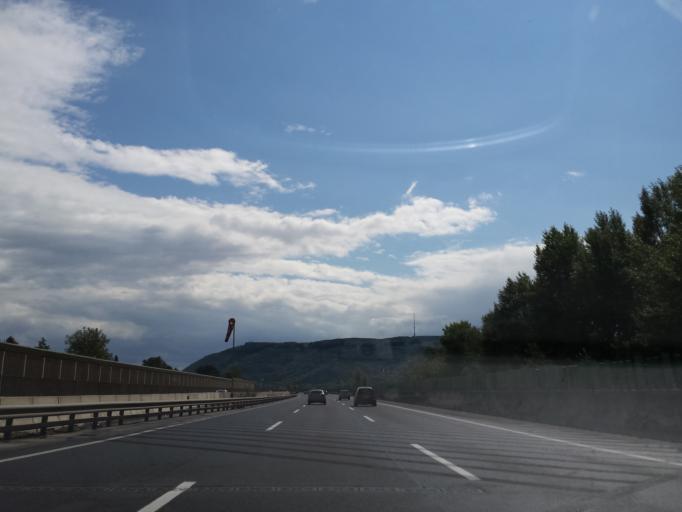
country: AT
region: Lower Austria
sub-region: Politischer Bezirk Korneuburg
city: Langenzersdorf
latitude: 48.3111
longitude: 16.3452
